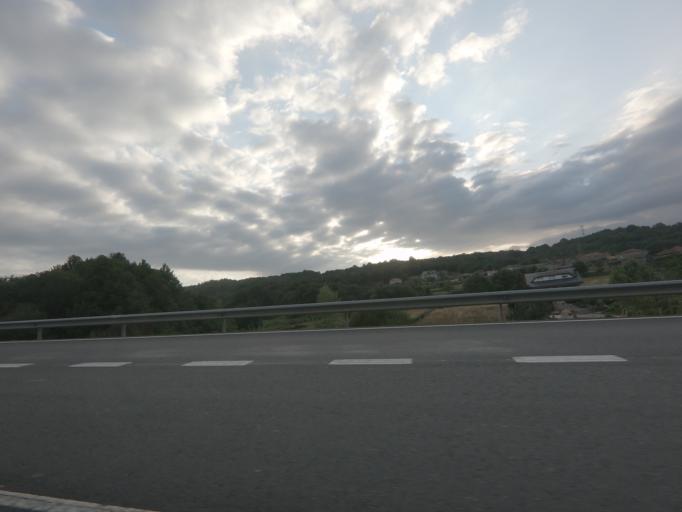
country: ES
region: Galicia
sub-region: Provincia de Ourense
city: Taboadela
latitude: 42.2468
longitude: -7.8419
